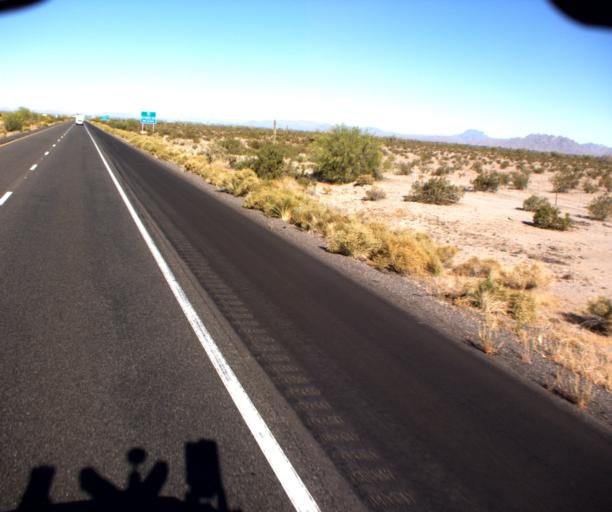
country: US
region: Arizona
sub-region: Maricopa County
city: Gila Bend
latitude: 32.9176
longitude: -112.6353
